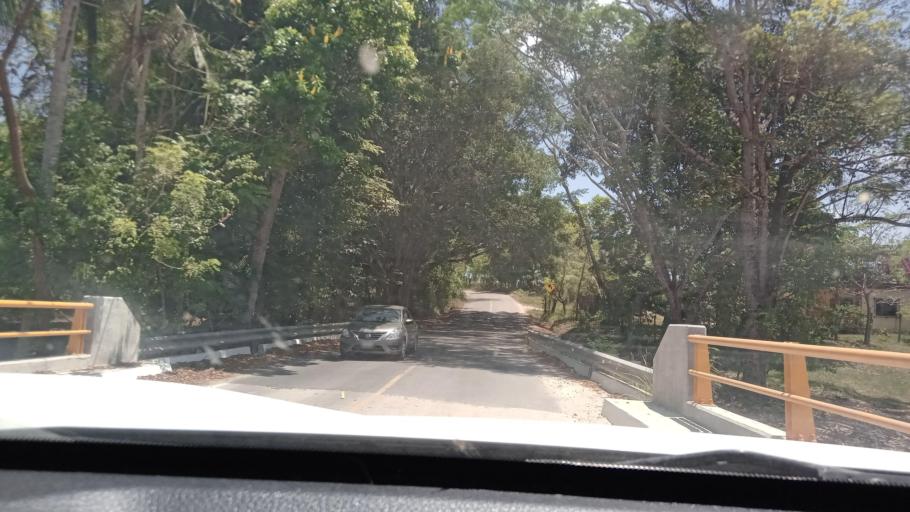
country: MX
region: Veracruz
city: Las Choapas
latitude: 17.7640
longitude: -94.1081
